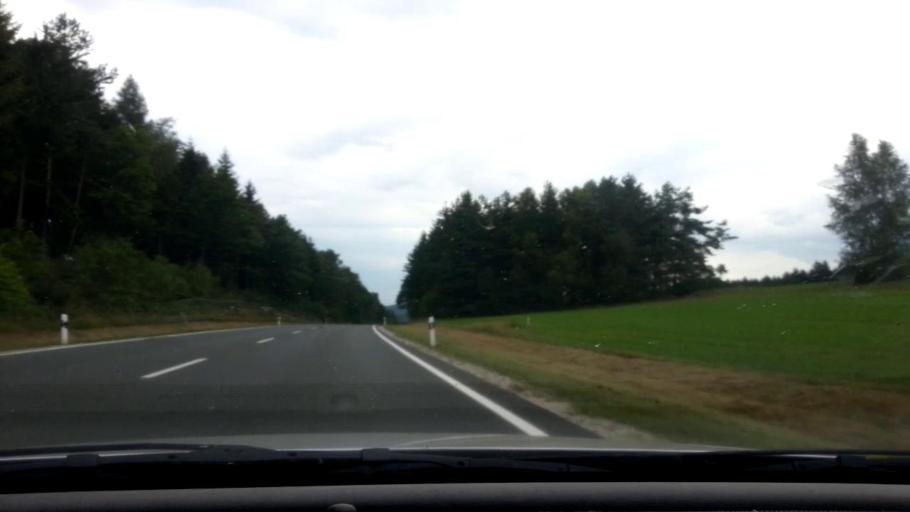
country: DE
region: Bavaria
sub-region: Upper Palatinate
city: Erbendorf
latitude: 49.8427
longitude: 12.0038
